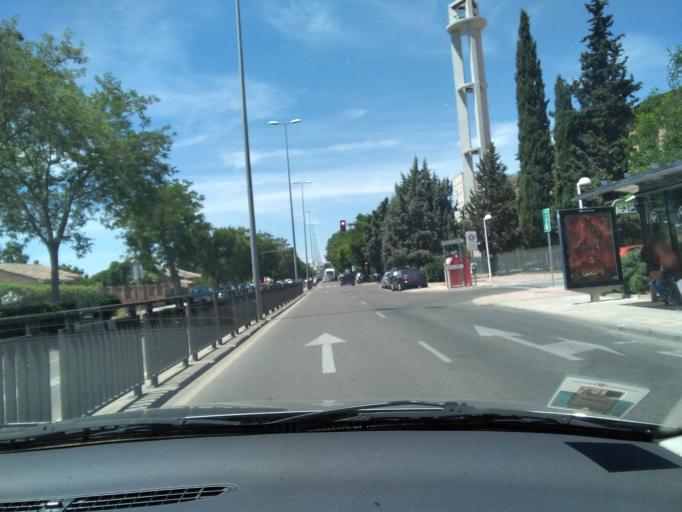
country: ES
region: Castille-La Mancha
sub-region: Province of Toledo
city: Toledo
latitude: 39.8703
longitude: -4.0339
